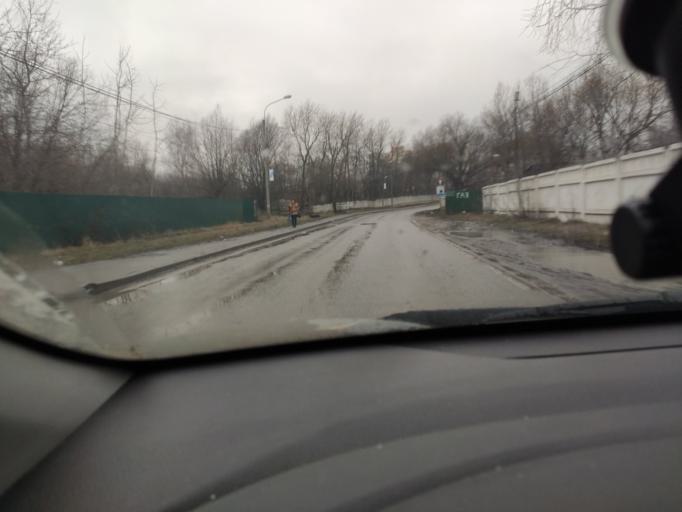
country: RU
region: Moscow
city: Zagor'ye
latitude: 55.5634
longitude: 37.6488
